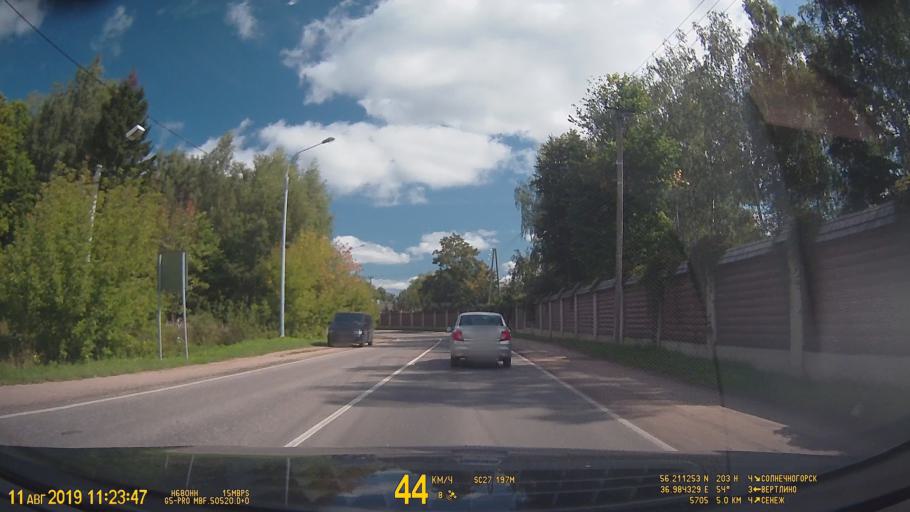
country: RU
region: Moskovskaya
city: Solnechnogorsk
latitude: 56.2113
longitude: 36.9845
